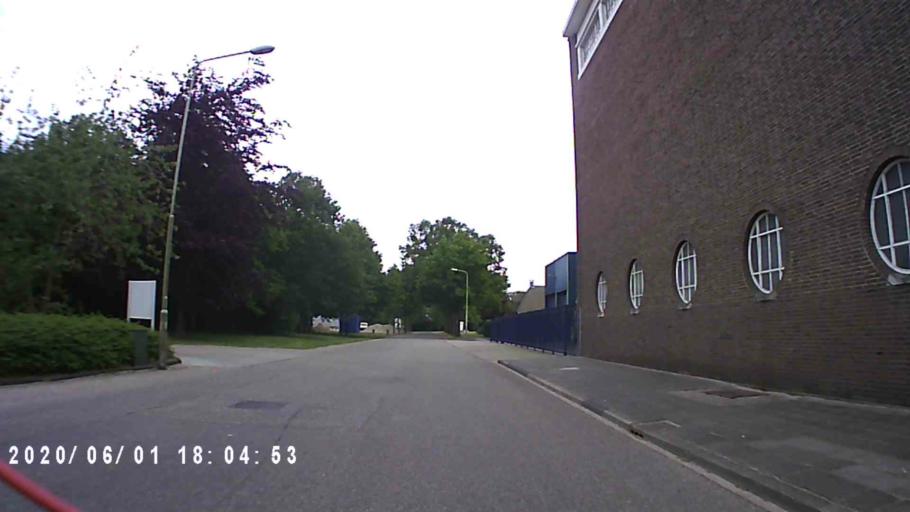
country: NL
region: Friesland
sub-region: Gemeente Tytsjerksteradiel
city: Sumar
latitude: 53.1811
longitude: 5.9941
